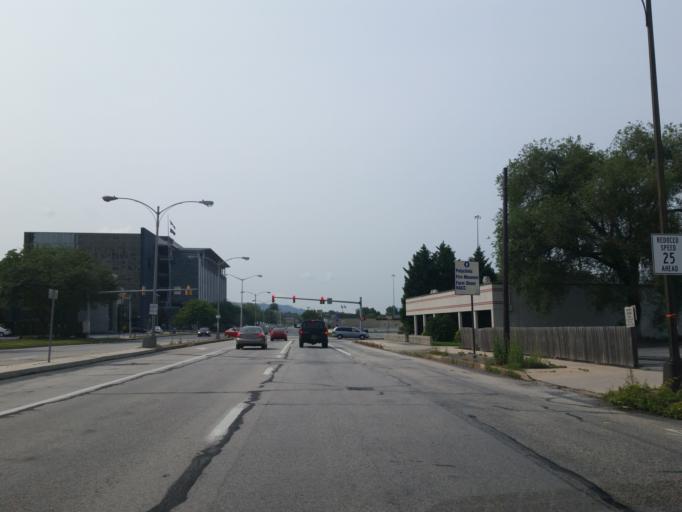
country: US
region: Pennsylvania
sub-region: Dauphin County
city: Harrisburg
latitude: 40.2694
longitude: -76.8820
